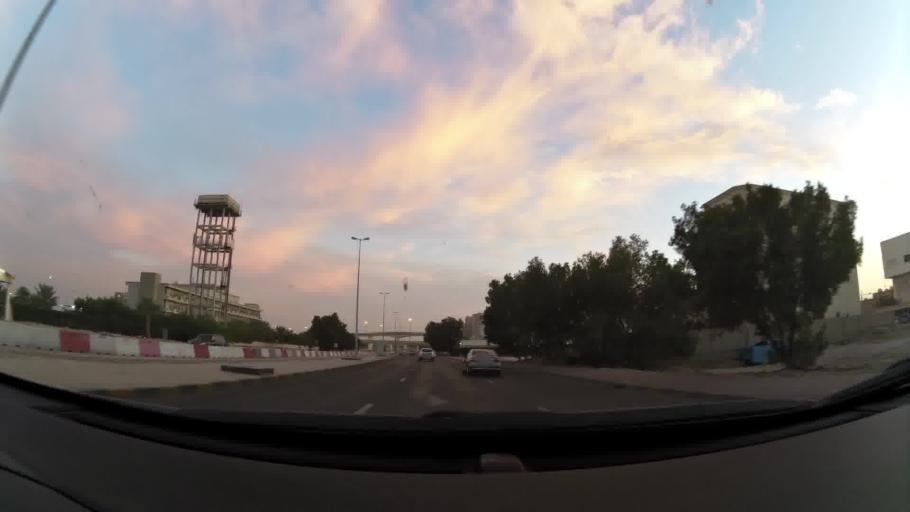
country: KW
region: Al Asimah
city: Ar Rabiyah
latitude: 29.3148
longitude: 47.8829
